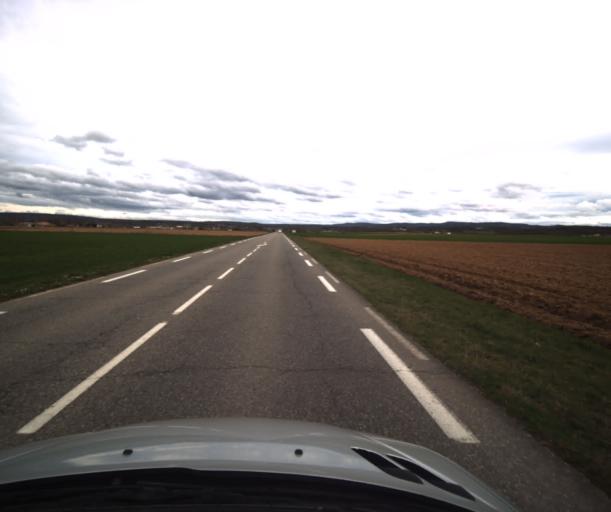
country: FR
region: Midi-Pyrenees
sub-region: Departement du Tarn-et-Garonne
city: Montricoux
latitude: 44.0738
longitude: 1.5821
